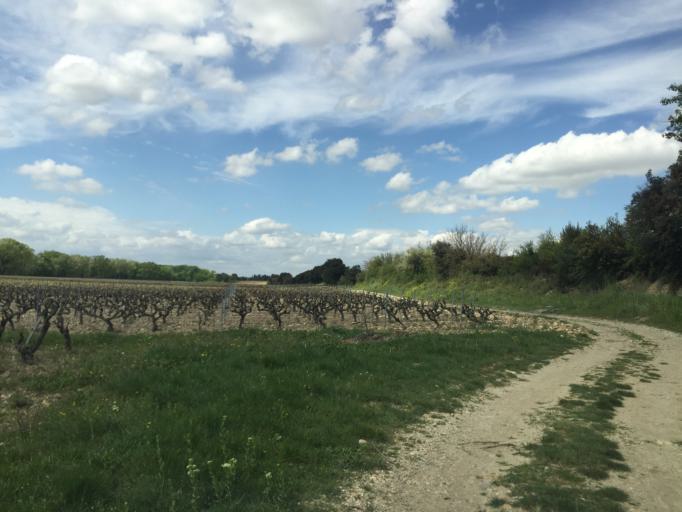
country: FR
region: Provence-Alpes-Cote d'Azur
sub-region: Departement du Vaucluse
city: Chateauneuf-du-Pape
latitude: 44.0443
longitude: 4.8243
